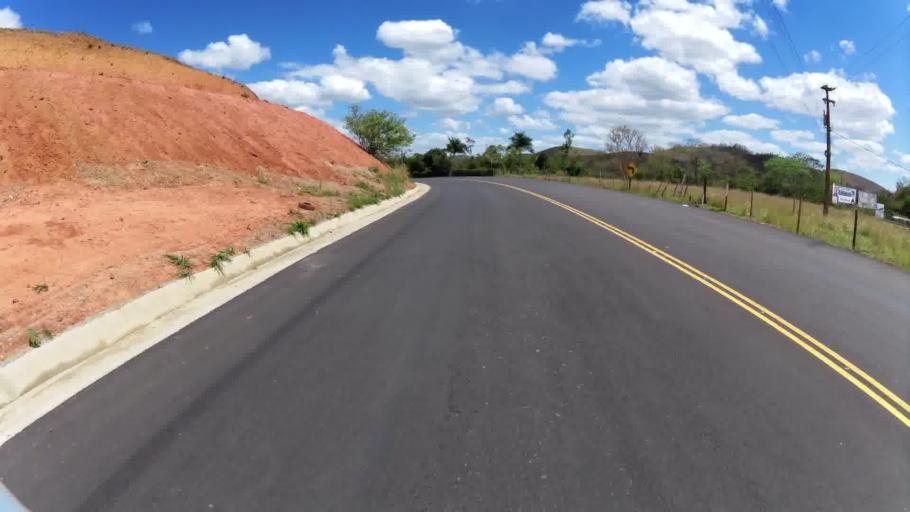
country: BR
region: Rio de Janeiro
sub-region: Itaperuna
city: Itaperuna
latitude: -21.2603
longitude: -41.7702
